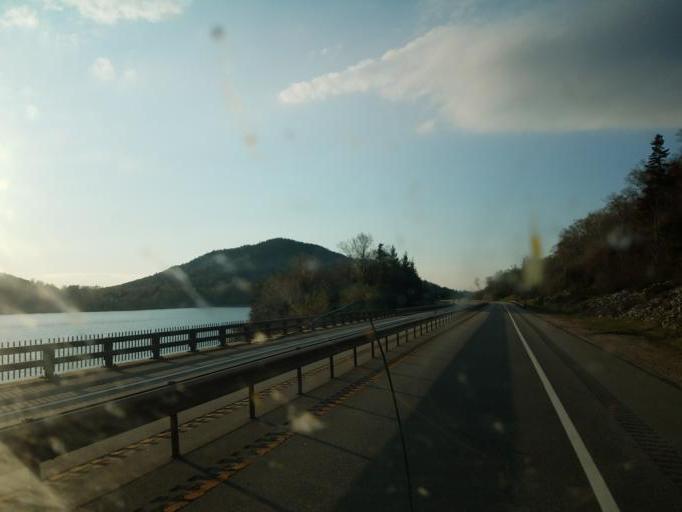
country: US
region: New Hampshire
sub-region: Grafton County
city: Deerfield
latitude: 44.1733
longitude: -71.6891
